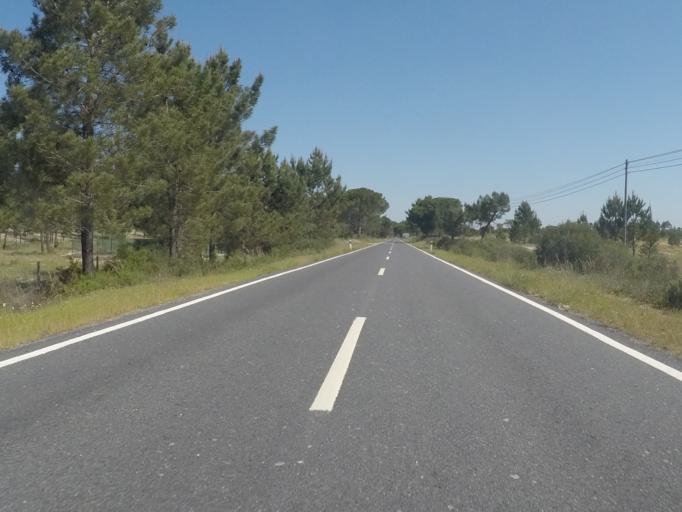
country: PT
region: Setubal
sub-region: Grandola
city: Grandola
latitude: 38.2902
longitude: -8.7265
